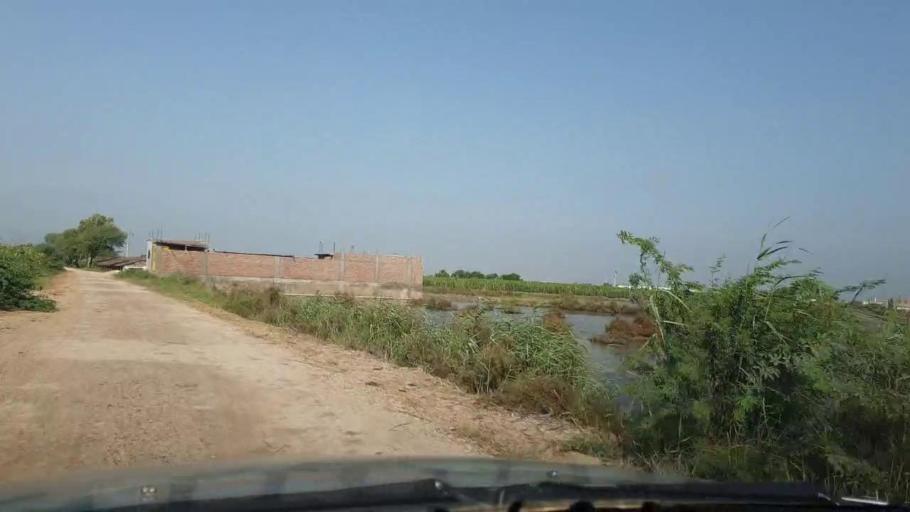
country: PK
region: Sindh
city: Matli
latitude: 25.0513
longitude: 68.6421
